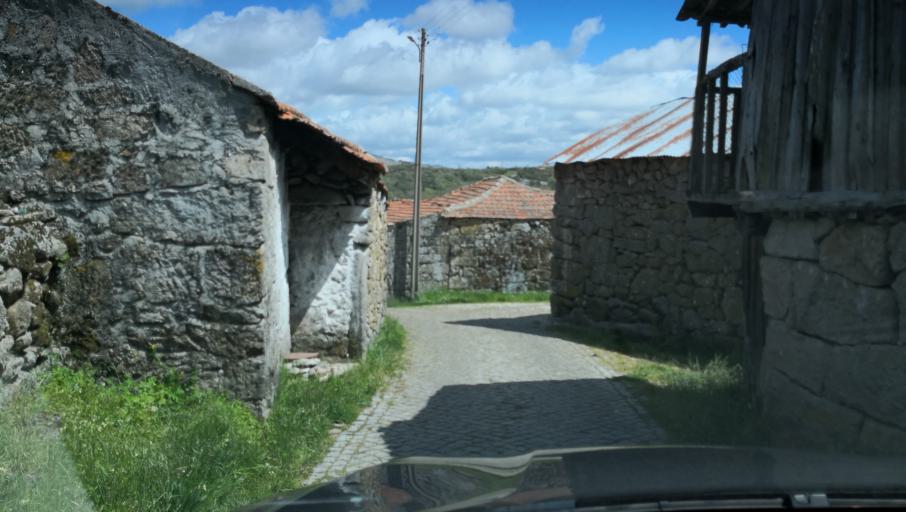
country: PT
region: Vila Real
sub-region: Vila Real
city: Vila Real
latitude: 41.4070
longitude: -7.7159
